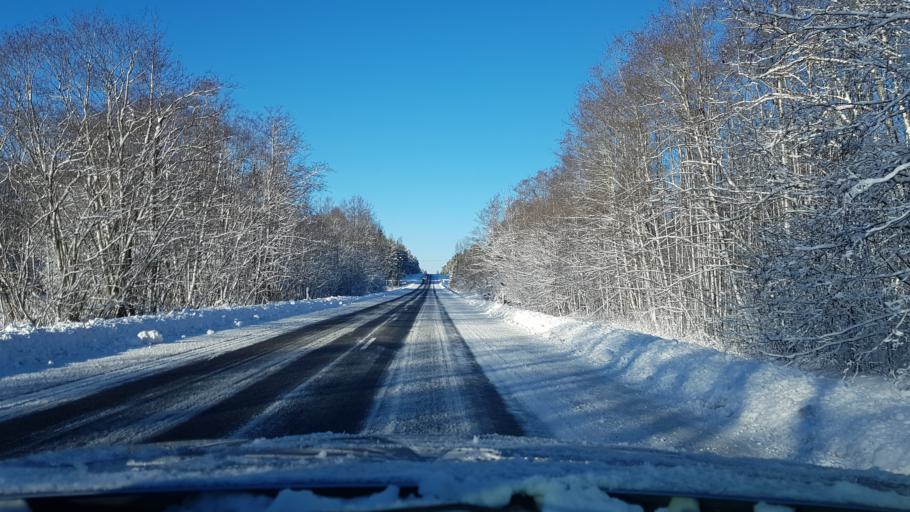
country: EE
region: Hiiumaa
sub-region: Kaerdla linn
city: Kardla
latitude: 58.9575
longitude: 22.8606
